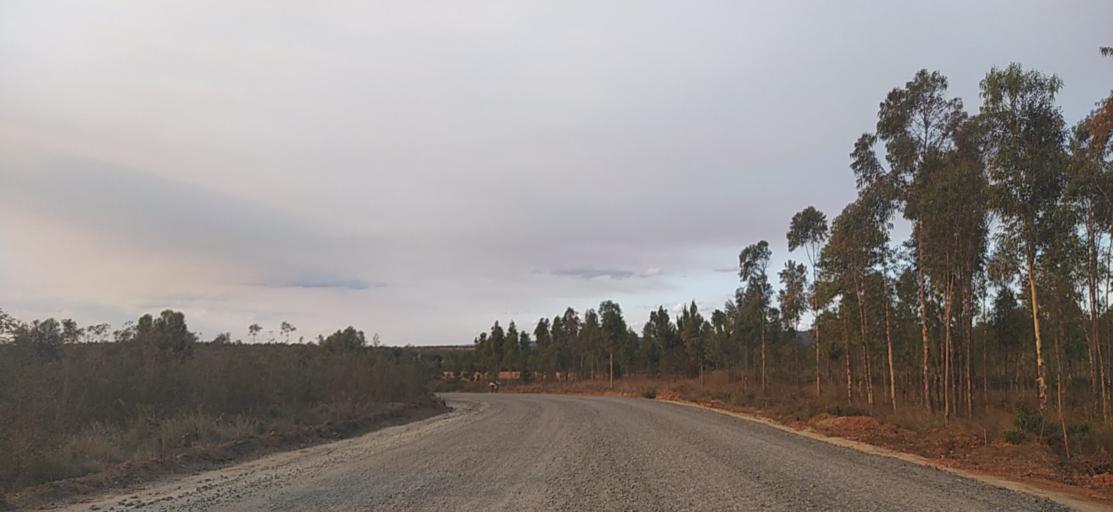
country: MG
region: Analamanga
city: Anjozorobe
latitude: -18.5030
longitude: 48.2678
